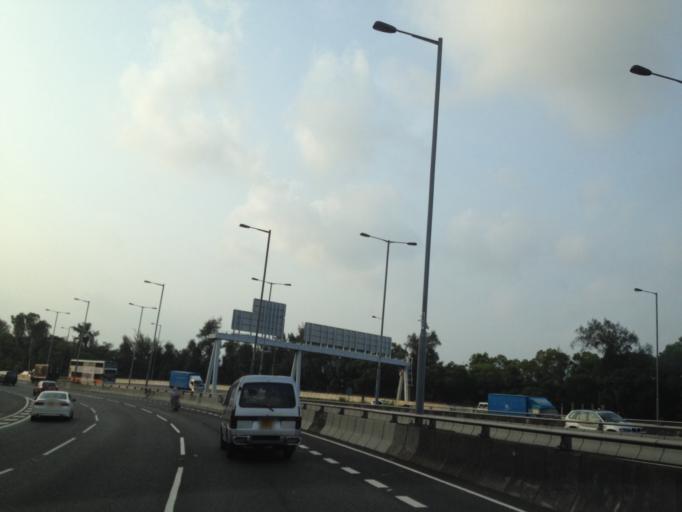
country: HK
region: Kowloon City
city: Kowloon
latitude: 22.2877
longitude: 114.2211
